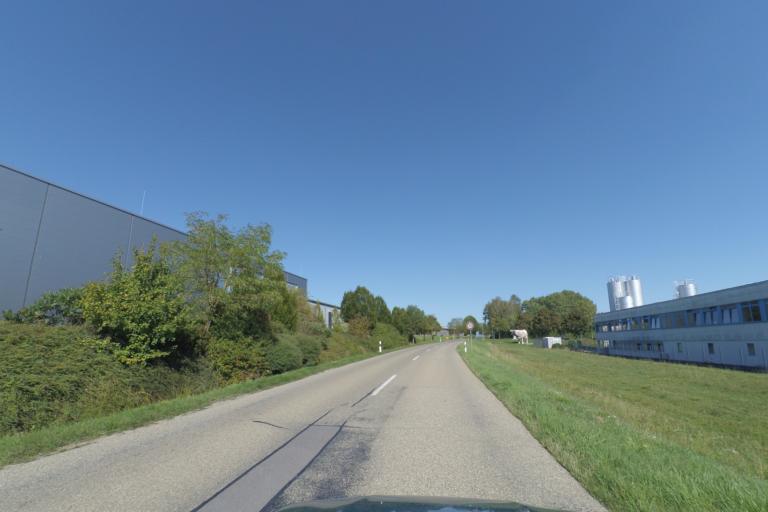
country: DE
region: Baden-Wuerttemberg
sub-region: Regierungsbezirk Stuttgart
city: Schrozberg
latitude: 49.3463
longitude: 9.9602
